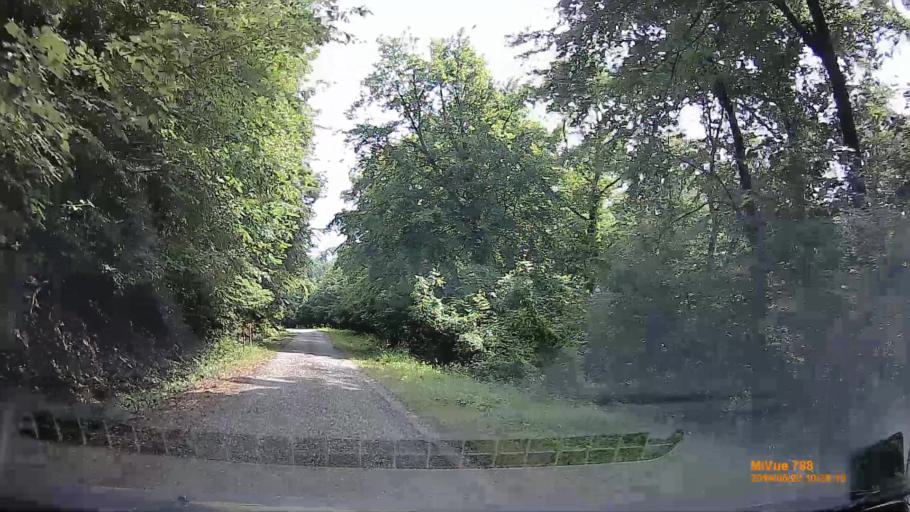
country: HU
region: Baranya
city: Mecseknadasd
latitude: 46.2059
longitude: 18.4932
